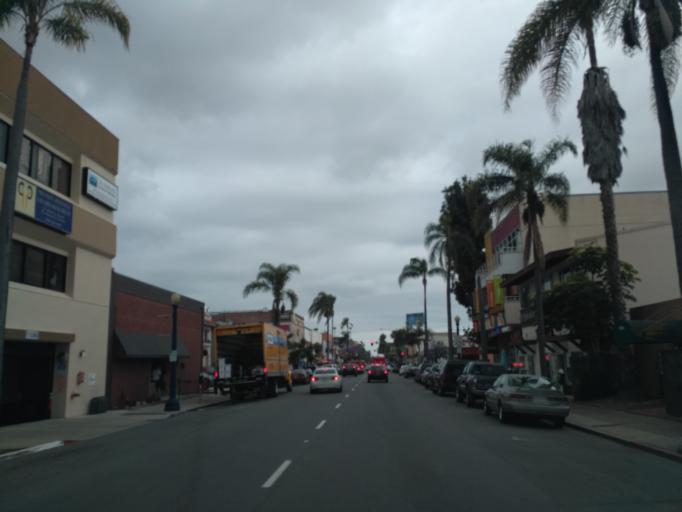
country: US
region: California
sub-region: San Diego County
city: San Diego
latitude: 32.7496
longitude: -117.1616
